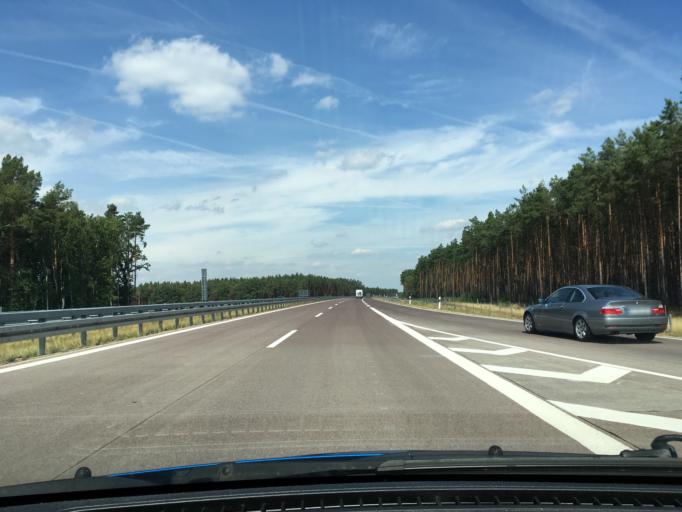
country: DE
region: Mecklenburg-Vorpommern
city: Ludwigslust
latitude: 53.3462
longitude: 11.5185
